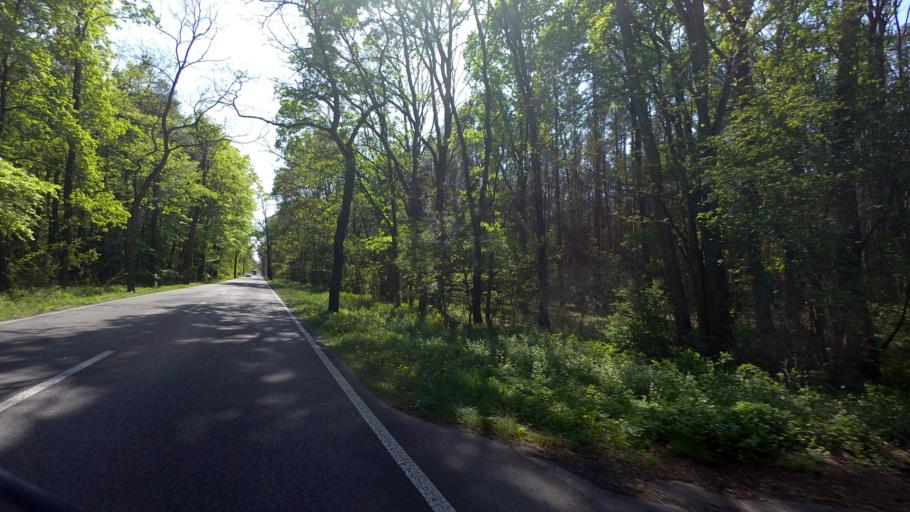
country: DE
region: Brandenburg
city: Tauche
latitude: 52.1087
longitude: 14.1856
